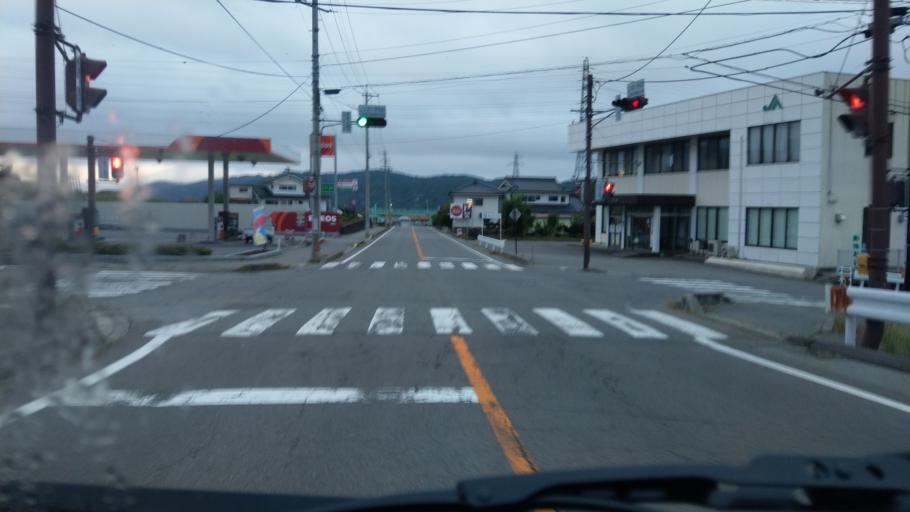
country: JP
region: Nagano
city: Komoro
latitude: 36.3398
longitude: 138.4187
